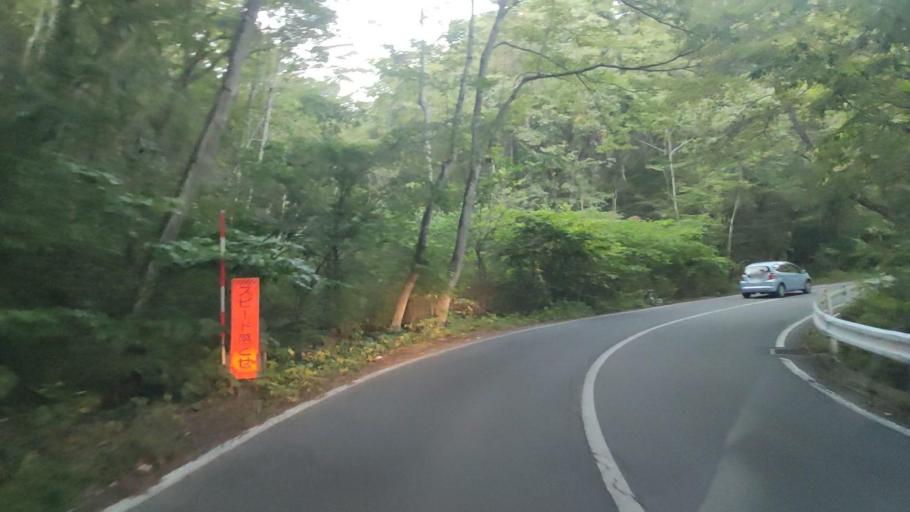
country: JP
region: Nagano
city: Komoro
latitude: 36.3815
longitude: 138.5909
